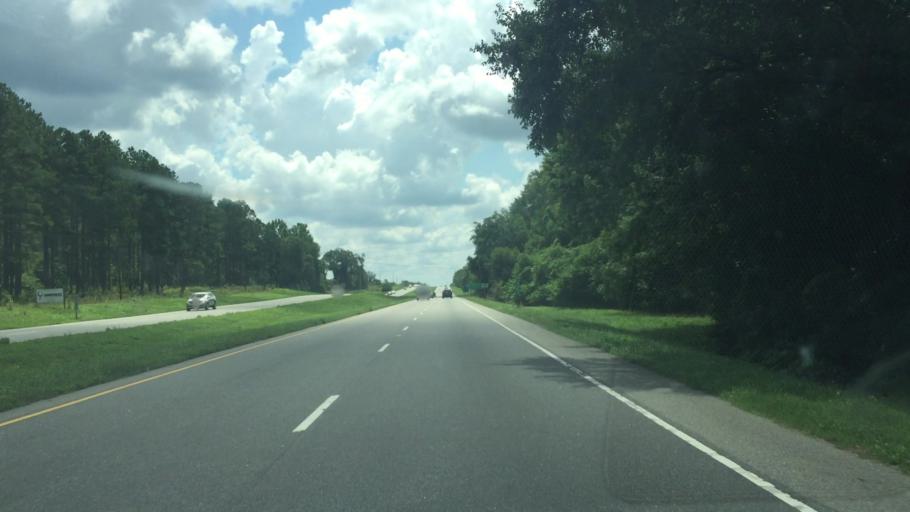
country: US
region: North Carolina
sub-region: Richmond County
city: Hamlet
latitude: 34.8552
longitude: -79.6244
